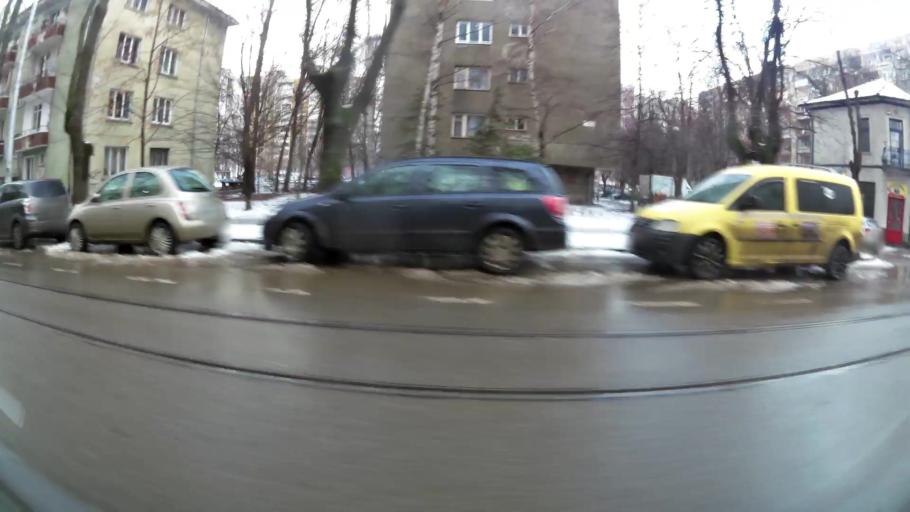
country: BG
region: Sofia-Capital
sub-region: Stolichna Obshtina
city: Sofia
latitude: 42.7072
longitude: 23.2912
